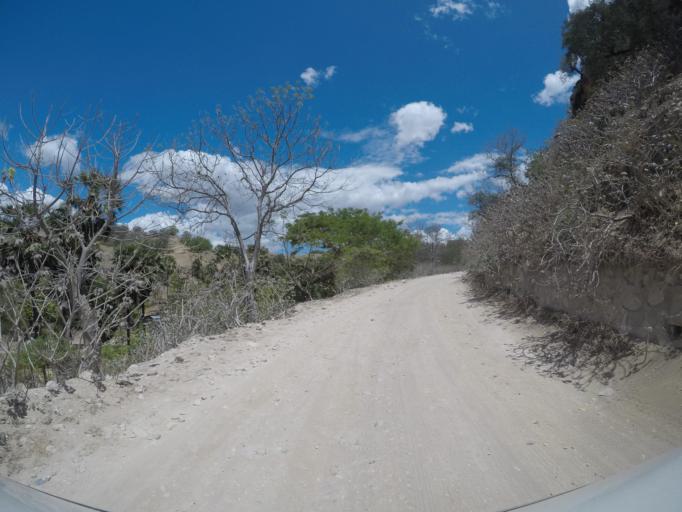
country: TL
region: Baucau
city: Baucau
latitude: -8.4735
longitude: 126.6025
